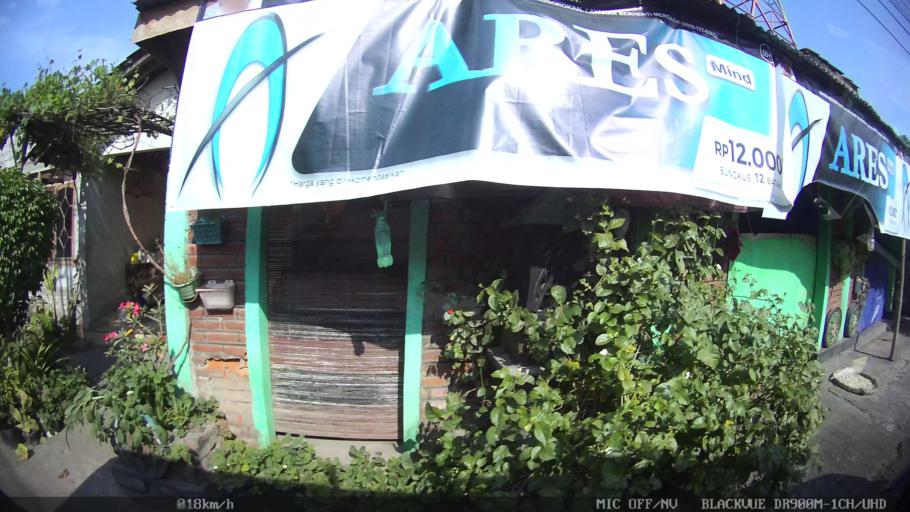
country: ID
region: Daerah Istimewa Yogyakarta
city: Kasihan
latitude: -7.8418
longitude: 110.3327
